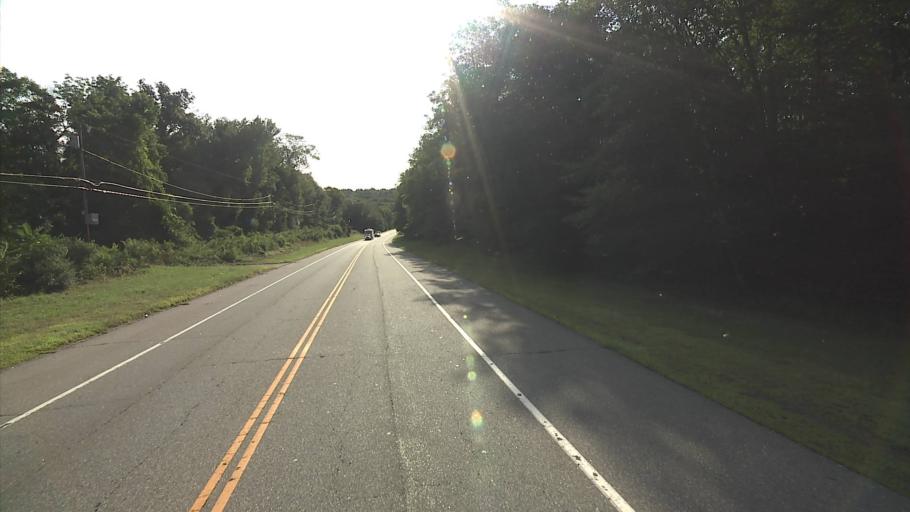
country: US
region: Connecticut
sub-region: New London County
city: Preston City
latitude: 41.4669
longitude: -71.9216
